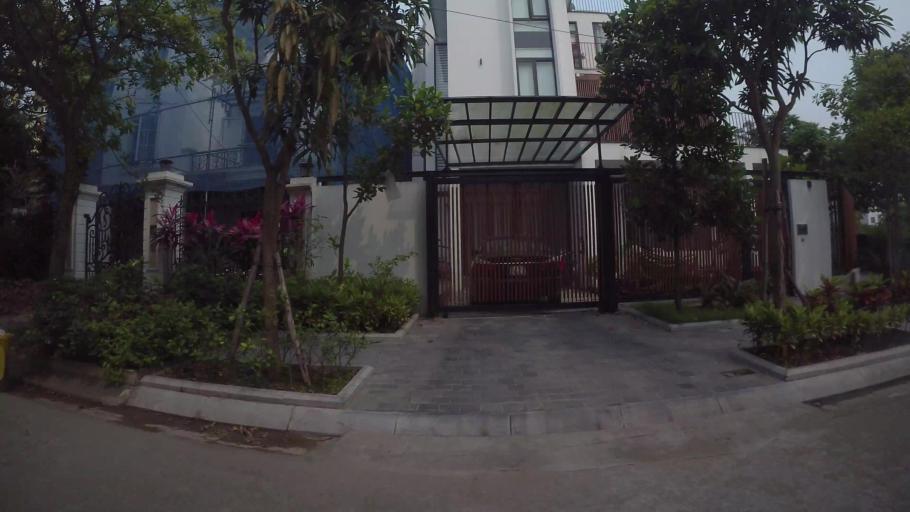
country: VN
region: Ha Noi
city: Trau Quy
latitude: 21.0579
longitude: 105.9104
